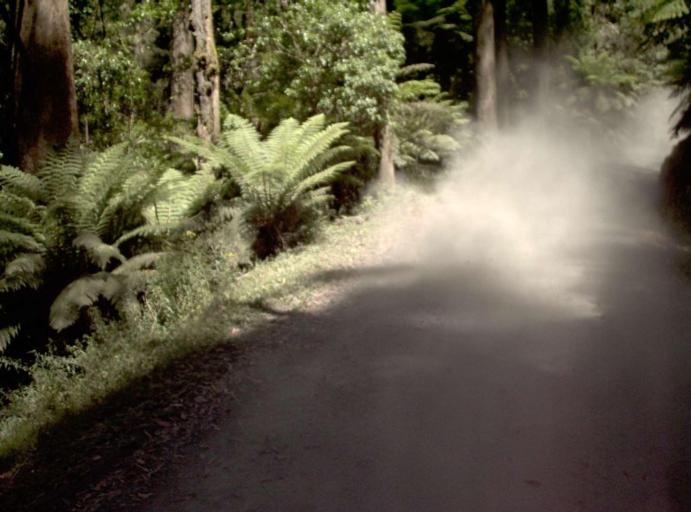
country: AU
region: Victoria
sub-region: Yarra Ranges
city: Millgrove
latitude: -37.6963
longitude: 145.7211
